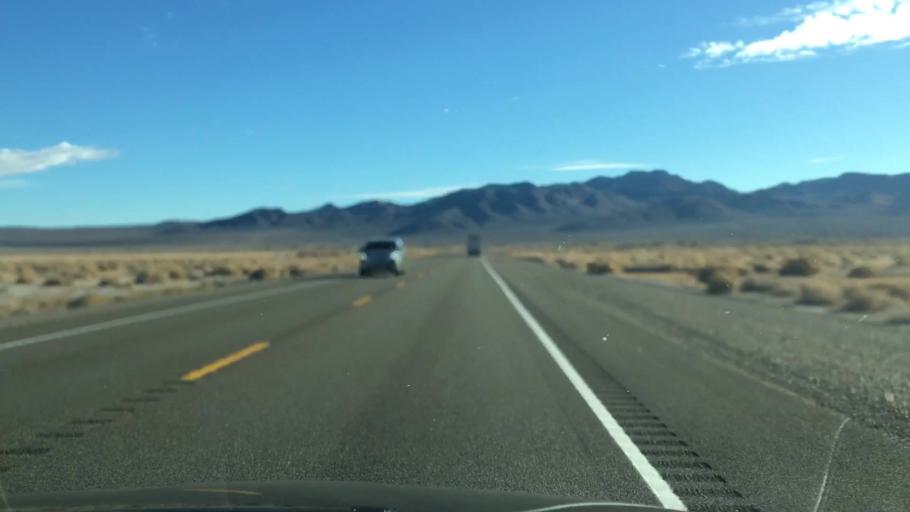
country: US
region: Nevada
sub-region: Mineral County
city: Hawthorne
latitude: 38.2763
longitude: -118.0985
